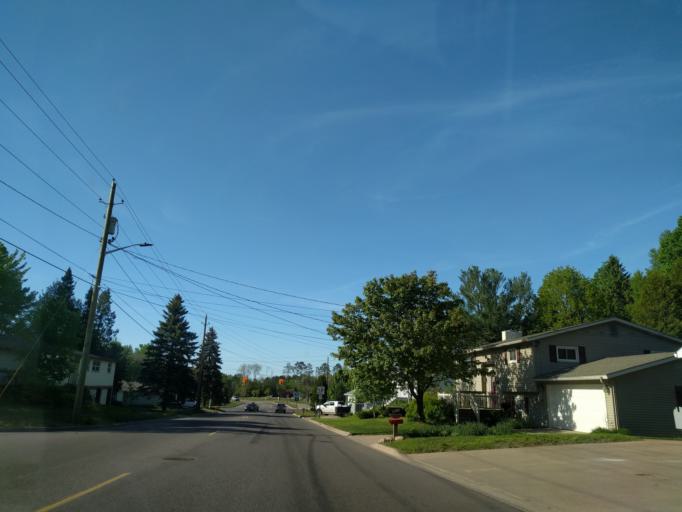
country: US
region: Michigan
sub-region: Marquette County
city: Trowbridge Park
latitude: 46.5558
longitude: -87.4197
